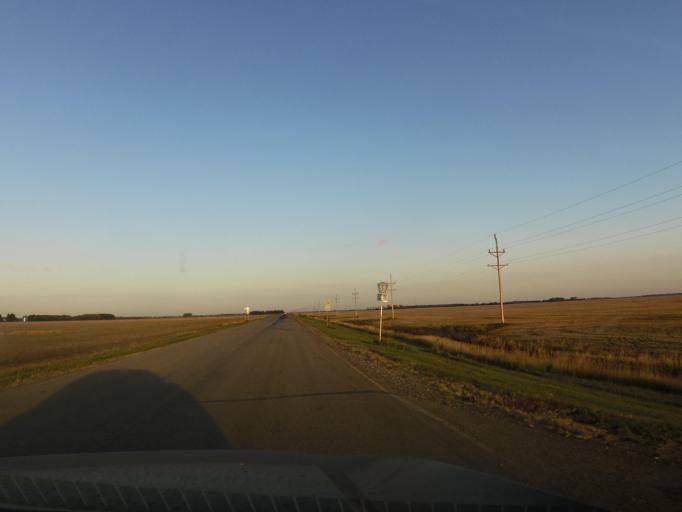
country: CA
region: Manitoba
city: Altona
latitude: 48.9633
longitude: -97.6234
